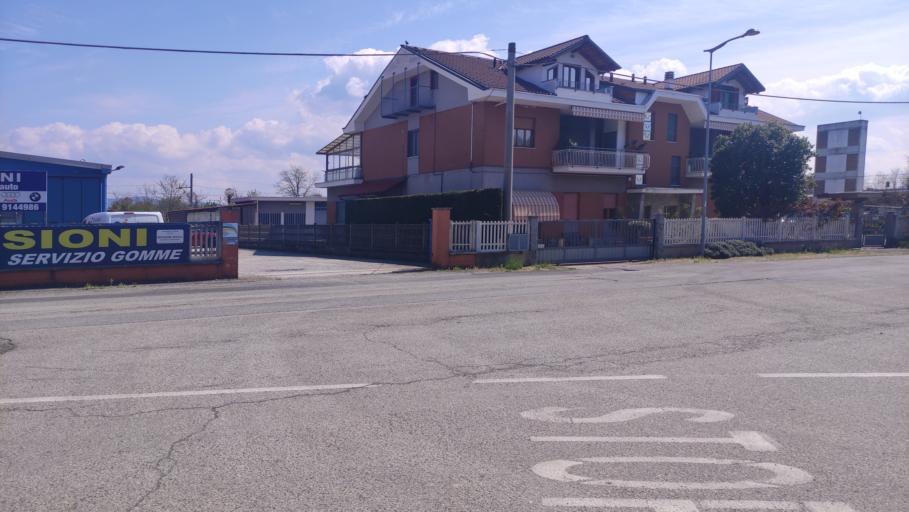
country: IT
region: Piedmont
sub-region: Provincia di Torino
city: Volpiano
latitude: 45.1894
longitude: 7.7739
